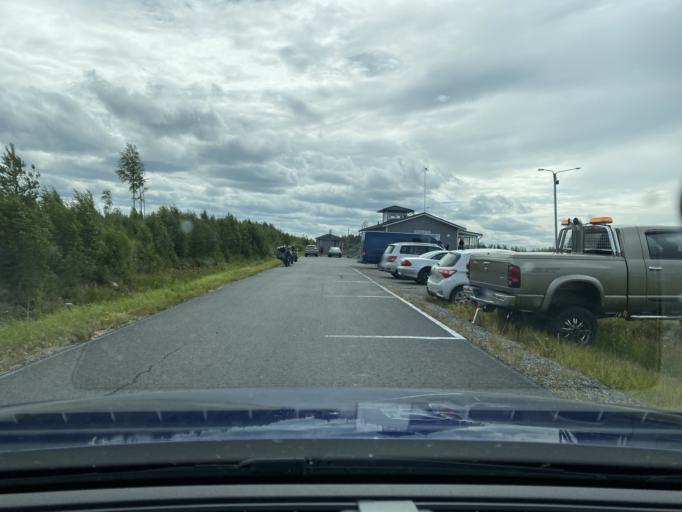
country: FI
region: Southern Ostrobothnia
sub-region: Seinaejoki
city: Jurva
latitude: 62.6220
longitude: 22.0325
